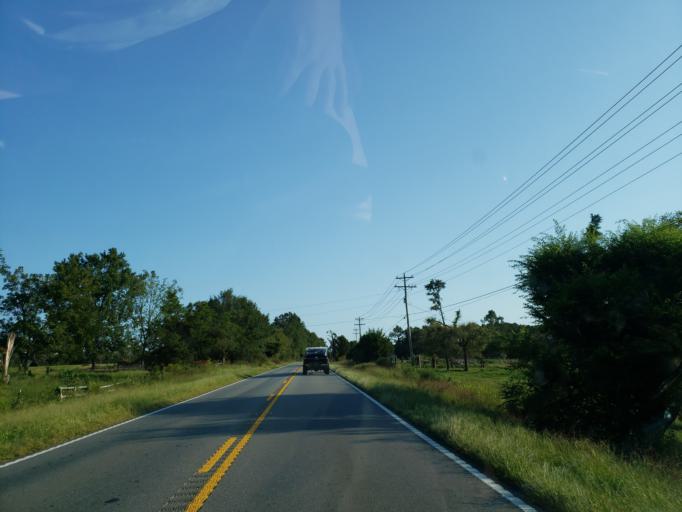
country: US
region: Georgia
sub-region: Murray County
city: Chatsworth
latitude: 34.7990
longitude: -84.8235
